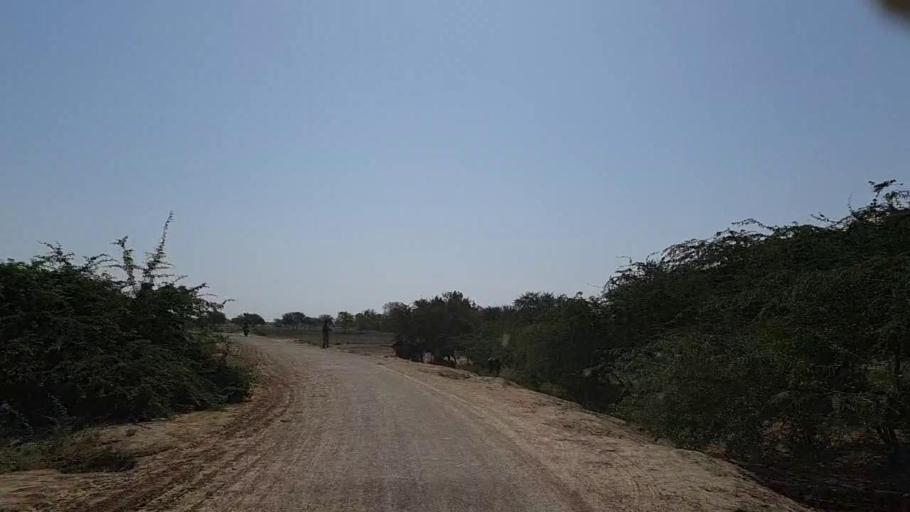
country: PK
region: Sindh
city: Mirpur Batoro
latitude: 24.6843
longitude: 68.2831
